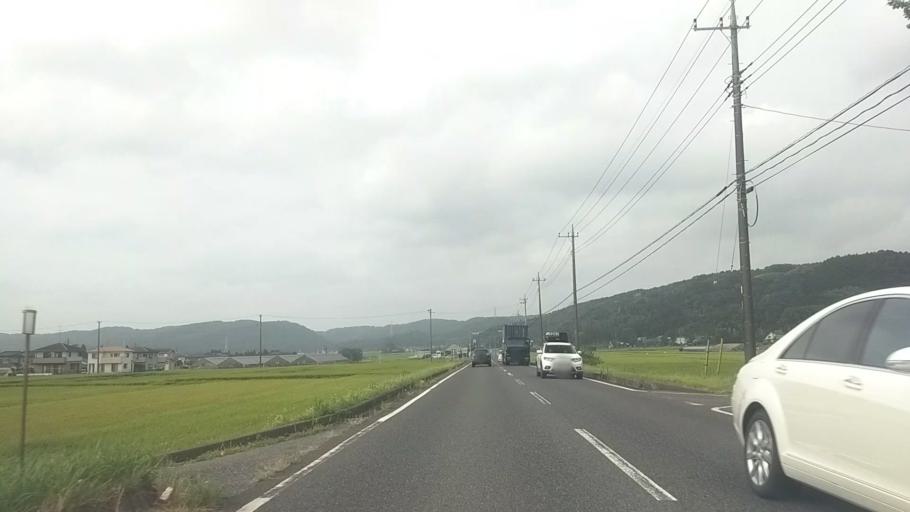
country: JP
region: Chiba
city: Kimitsu
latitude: 35.2880
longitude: 139.9903
